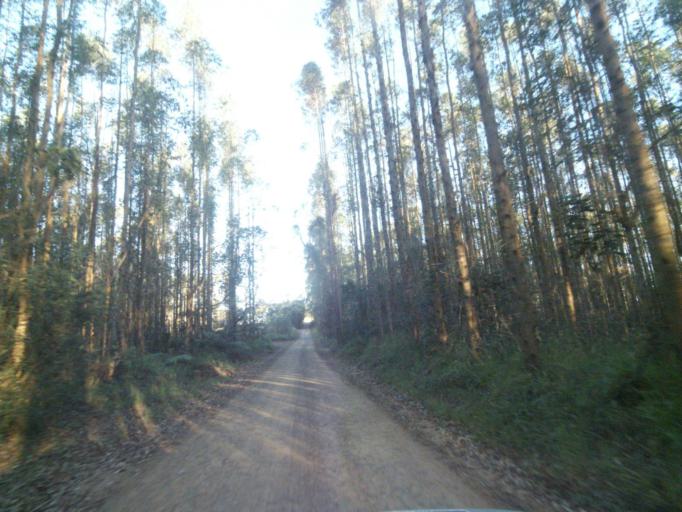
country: BR
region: Parana
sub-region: Telemaco Borba
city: Telemaco Borba
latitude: -24.4970
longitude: -50.6003
